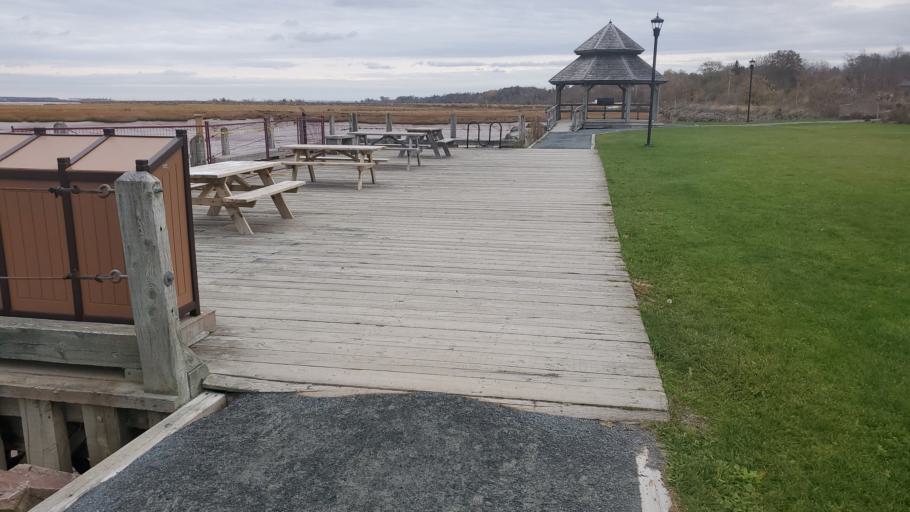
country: CA
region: Nova Scotia
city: Wolfville
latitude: 45.0927
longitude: -64.3590
